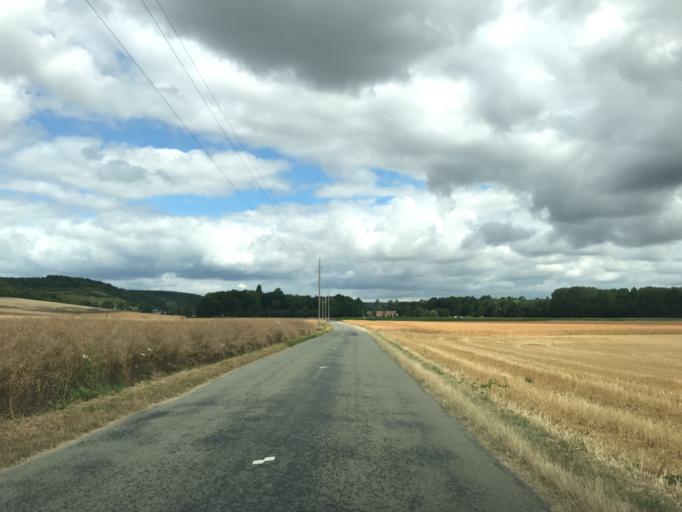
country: FR
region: Haute-Normandie
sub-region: Departement de l'Eure
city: Houlbec-Cocherel
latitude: 49.0556
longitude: 1.2997
